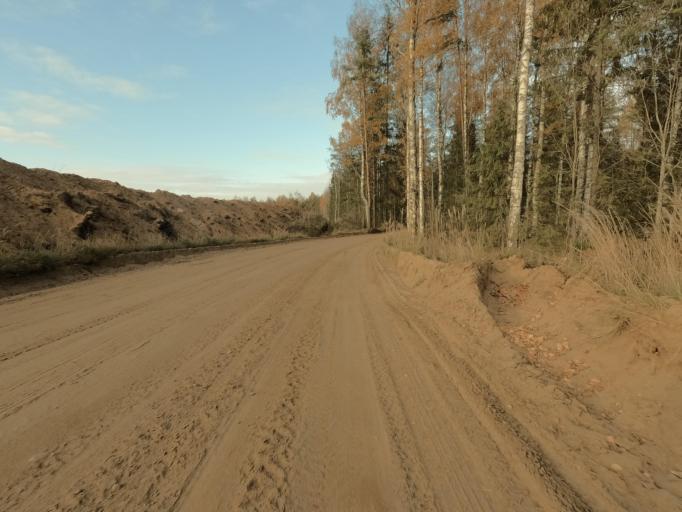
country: RU
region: Leningrad
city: Priladozhskiy
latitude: 59.7370
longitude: 31.3170
